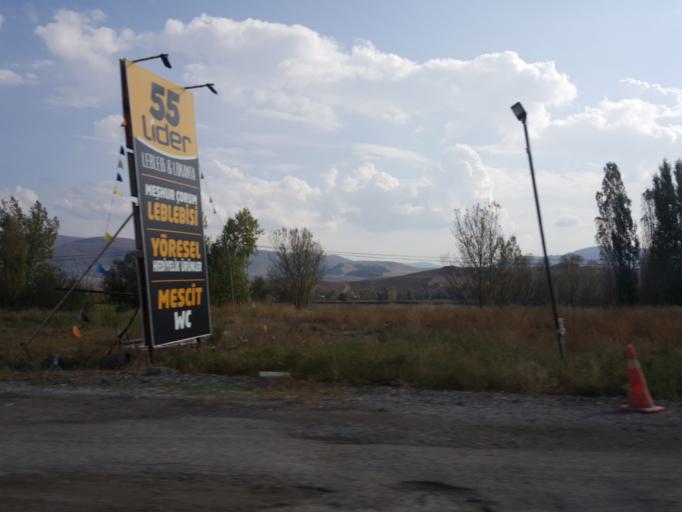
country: TR
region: Corum
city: Seydim
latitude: 40.4296
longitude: 34.7872
